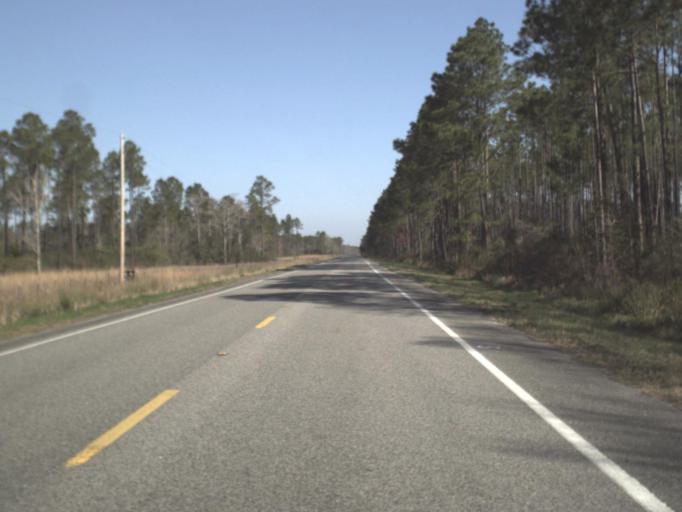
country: US
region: Florida
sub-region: Leon County
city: Woodville
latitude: 30.2347
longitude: -84.0427
